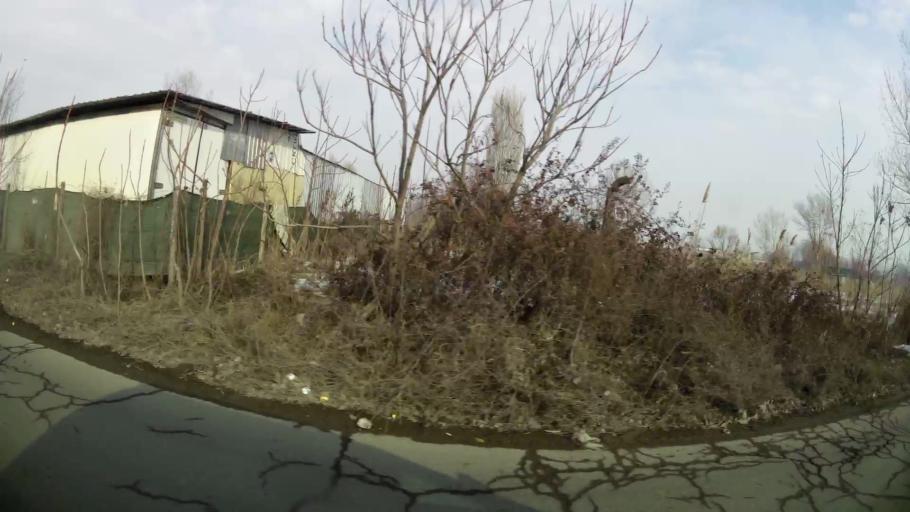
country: MK
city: Krushopek
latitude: 42.0139
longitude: 21.3726
